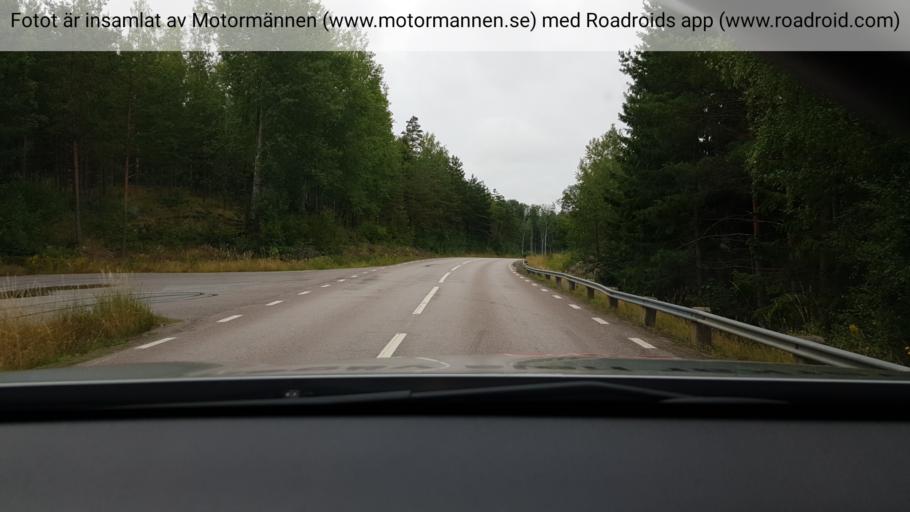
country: SE
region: Soedermanland
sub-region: Strangnas Kommun
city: Mariefred
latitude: 59.1936
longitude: 17.1844
